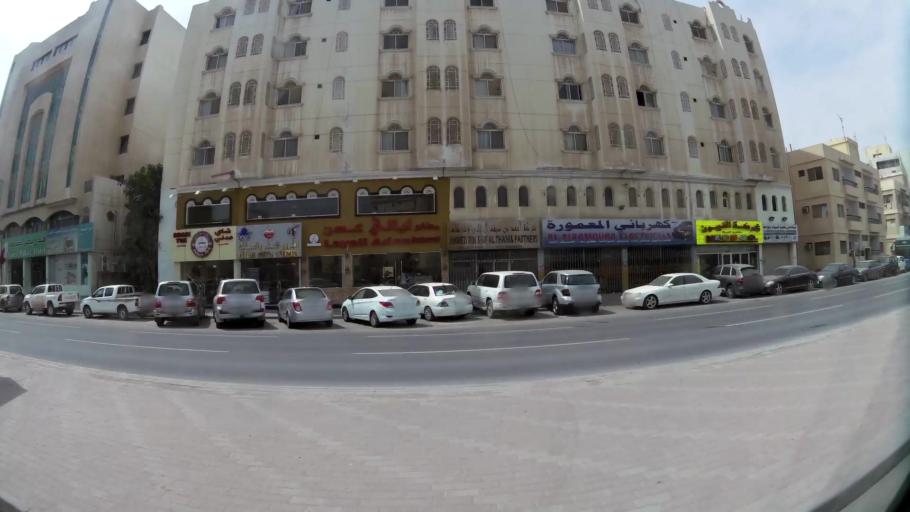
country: QA
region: Baladiyat ad Dawhah
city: Doha
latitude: 25.2810
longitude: 51.5444
